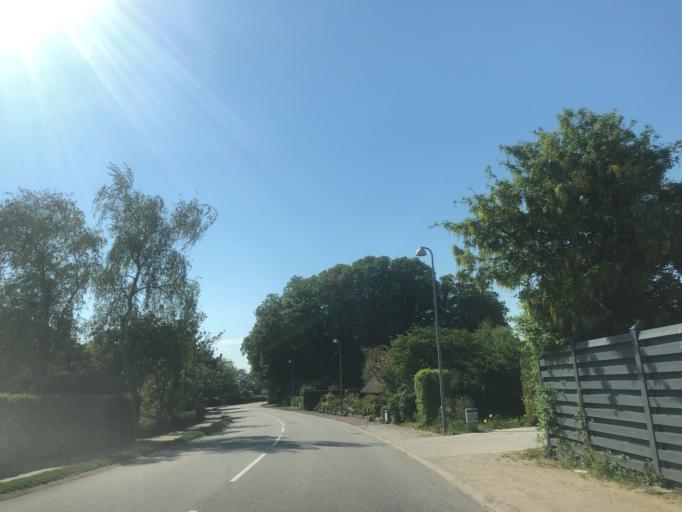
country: DK
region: Zealand
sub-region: Solrod Kommune
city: Havdrup
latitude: 55.5747
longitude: 12.0944
